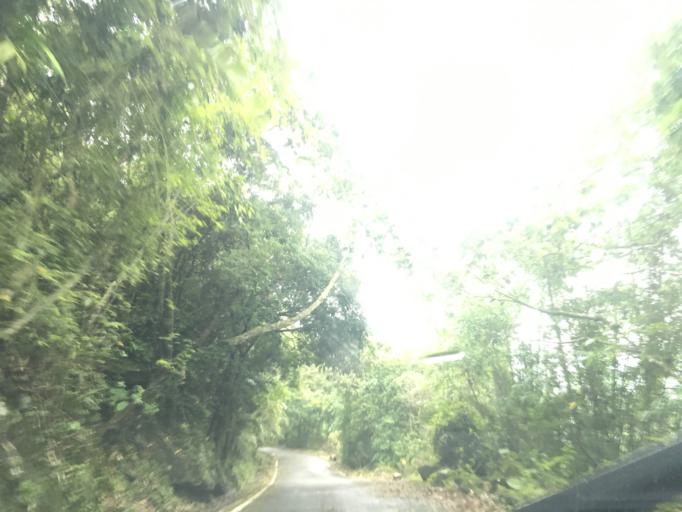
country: TW
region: Taiwan
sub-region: Yunlin
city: Douliu
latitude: 23.5692
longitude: 120.6396
